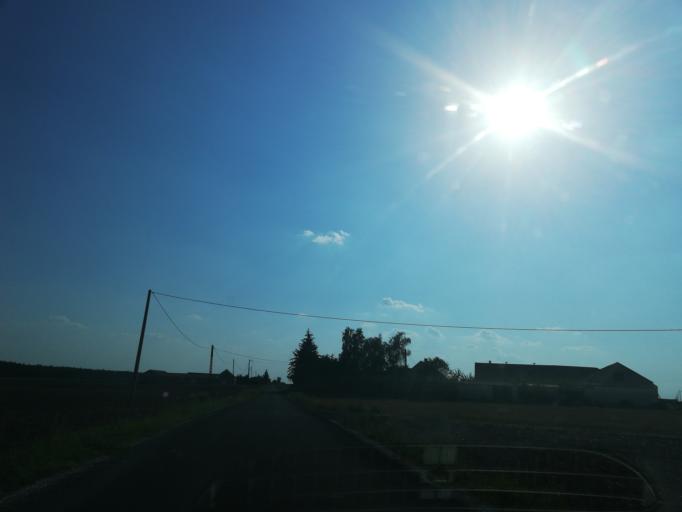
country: PL
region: Kujawsko-Pomorskie
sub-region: Powiat golubsko-dobrzynski
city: Kowalewo Pomorskie
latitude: 53.1107
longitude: 18.9070
